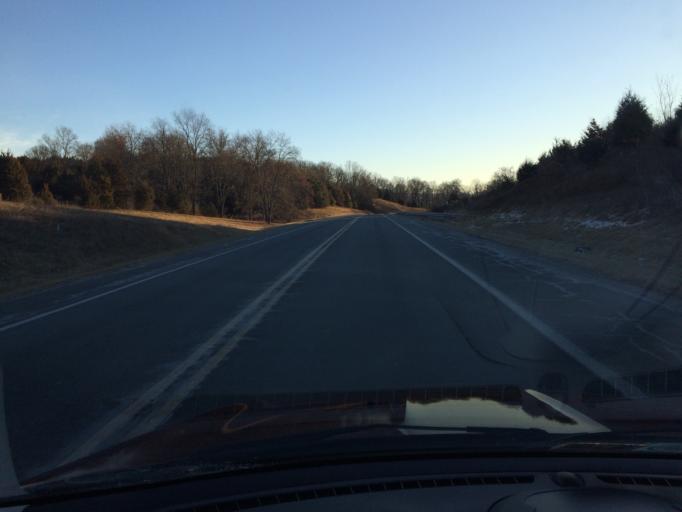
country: US
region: Virginia
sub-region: Augusta County
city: Verona
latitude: 38.1877
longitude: -79.0478
